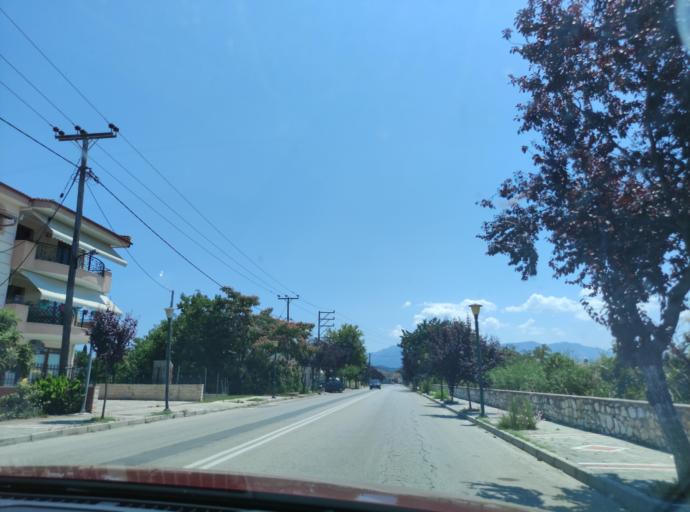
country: GR
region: East Macedonia and Thrace
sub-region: Nomos Kavalas
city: Keramoti
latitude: 40.8626
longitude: 24.7057
